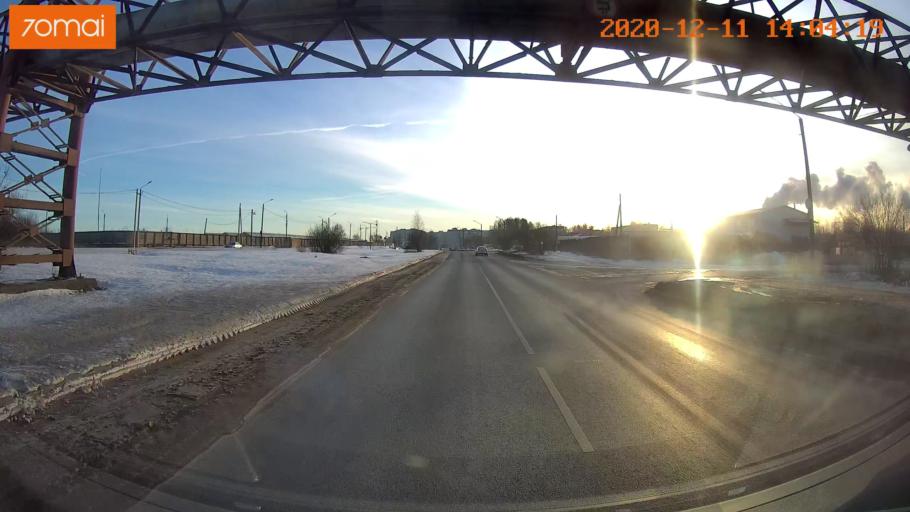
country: RU
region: Kostroma
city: Oktyabr'skiy
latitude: 57.7566
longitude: 41.0161
